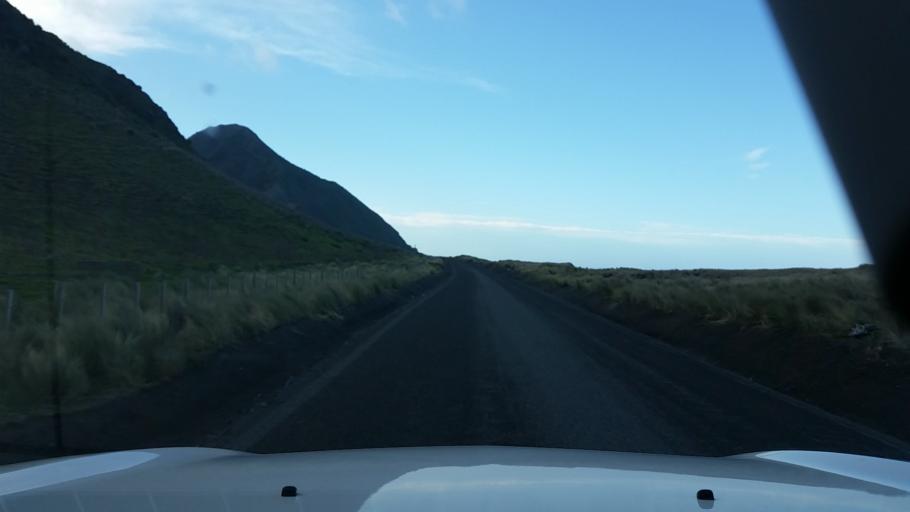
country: NZ
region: Wellington
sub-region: South Wairarapa District
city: Waipawa
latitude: -41.6023
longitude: 175.2473
